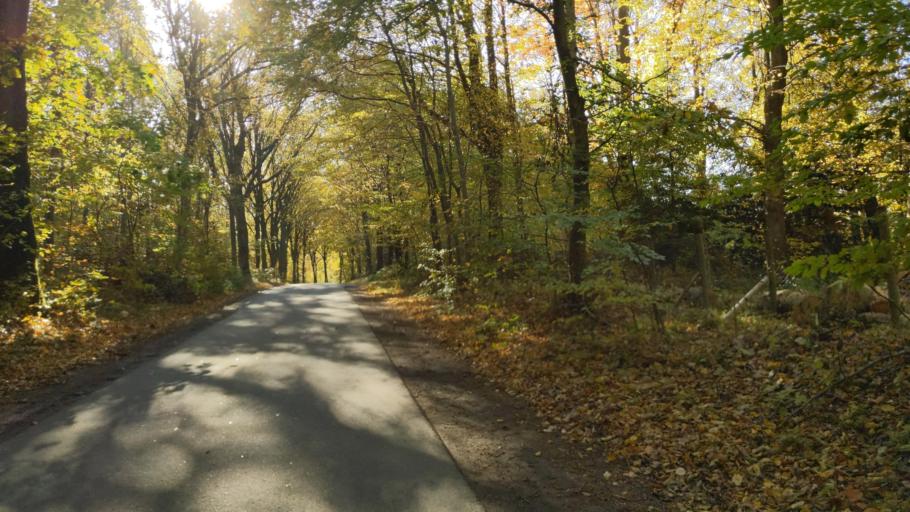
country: DE
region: Schleswig-Holstein
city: Eutin
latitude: 54.1512
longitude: 10.6501
